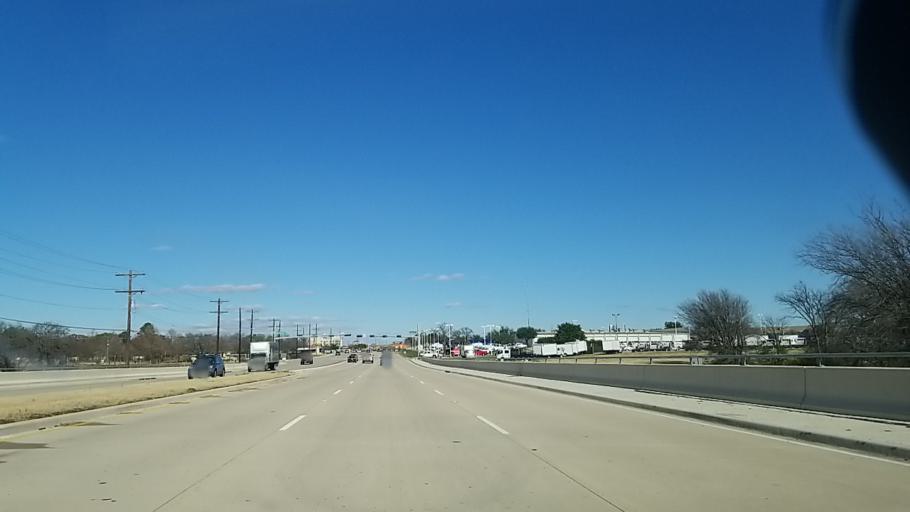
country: US
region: Texas
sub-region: Denton County
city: Corinth
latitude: 33.1678
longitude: -97.0908
